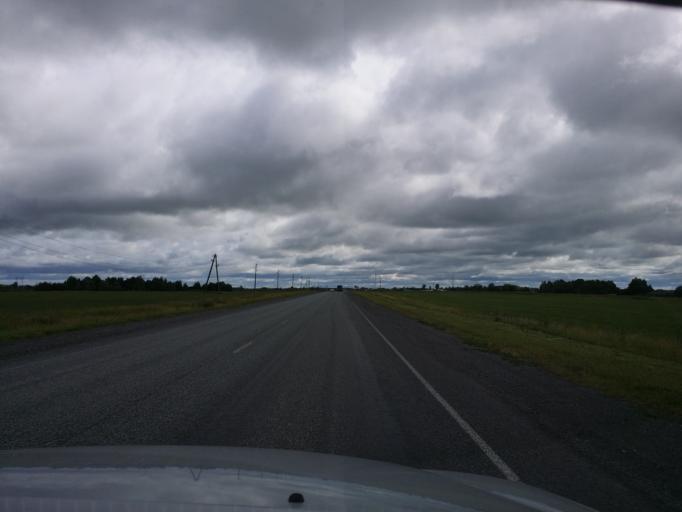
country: RU
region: Tjumen
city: Yarkovo
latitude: 57.2395
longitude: 66.7507
